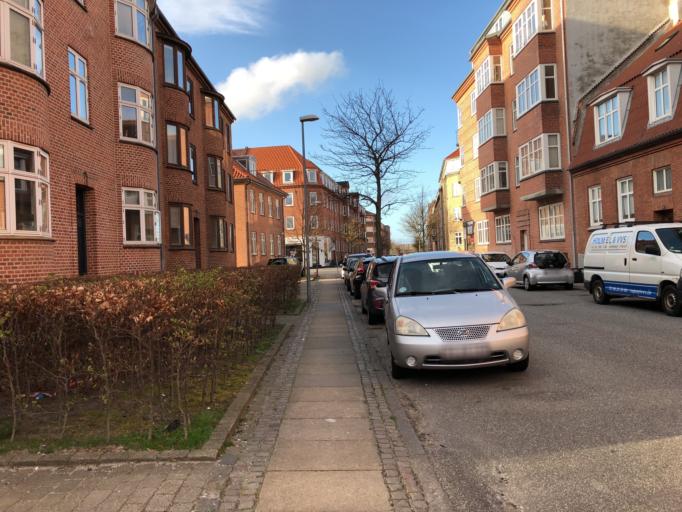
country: DK
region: North Denmark
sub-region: Alborg Kommune
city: Aalborg
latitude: 57.0536
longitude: 9.9014
